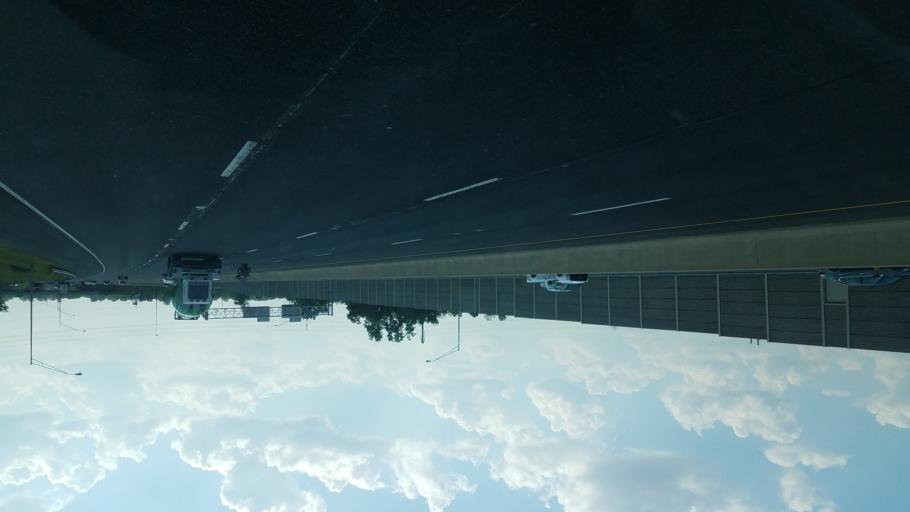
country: US
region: Indiana
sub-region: Allen County
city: Fort Wayne
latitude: 41.1745
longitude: -85.1034
